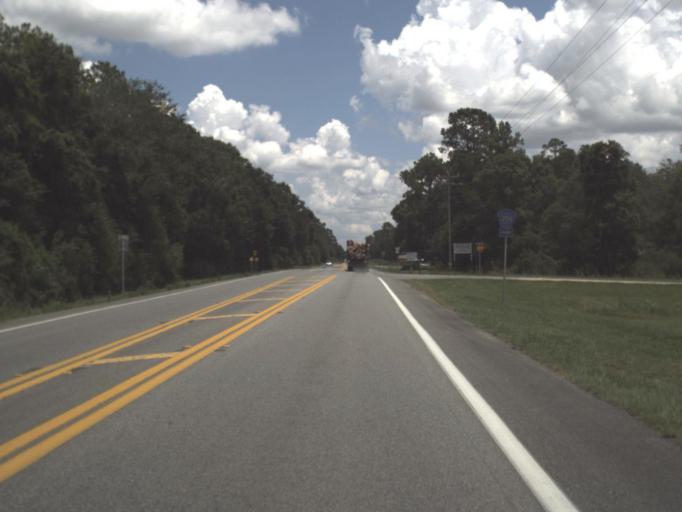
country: US
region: Florida
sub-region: Taylor County
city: Perry
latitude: 30.0869
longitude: -83.6543
